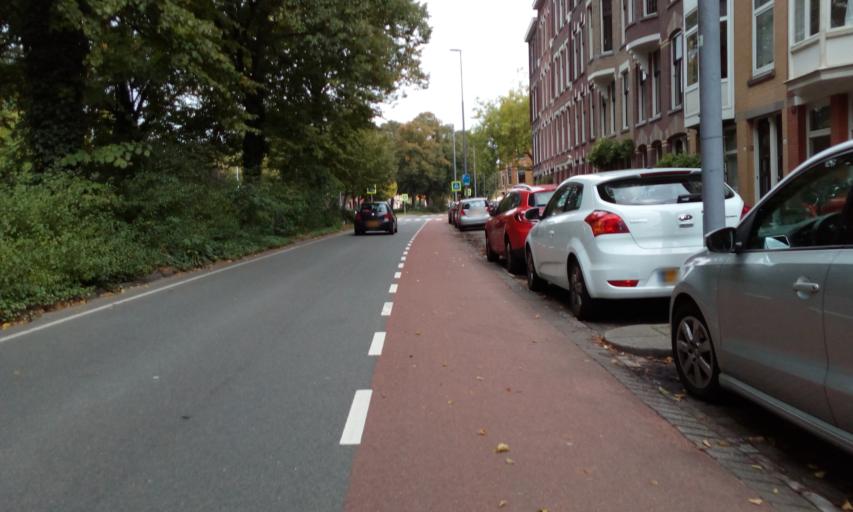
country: NL
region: South Holland
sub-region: Gemeente Rotterdam
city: Rotterdam
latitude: 51.9375
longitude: 4.4737
